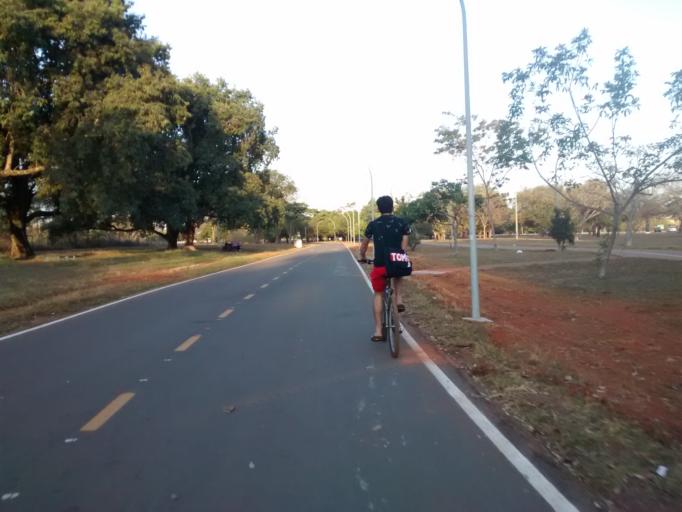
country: BR
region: Federal District
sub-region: Brasilia
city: Brasilia
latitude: -15.8031
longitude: -47.9094
